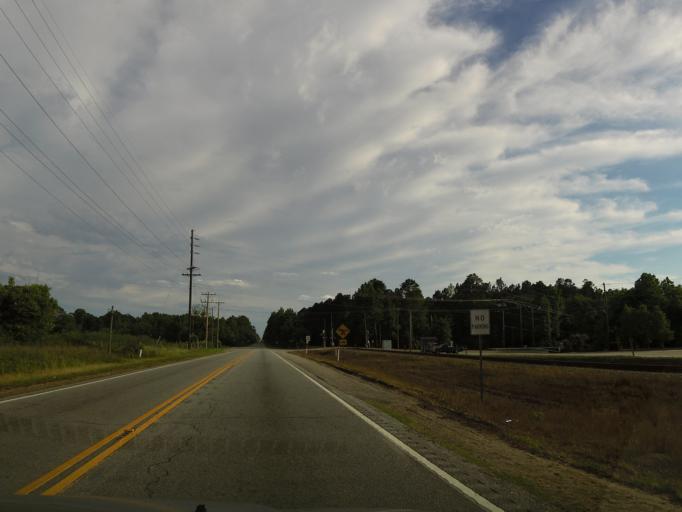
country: US
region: South Carolina
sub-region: Hampton County
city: Estill
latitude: 32.7271
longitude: -81.2420
